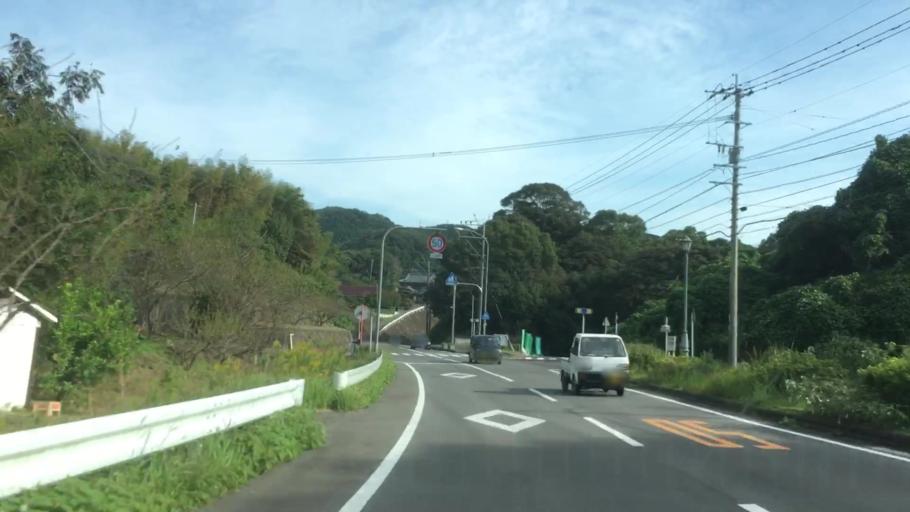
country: JP
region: Nagasaki
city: Sasebo
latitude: 32.9976
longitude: 129.6586
